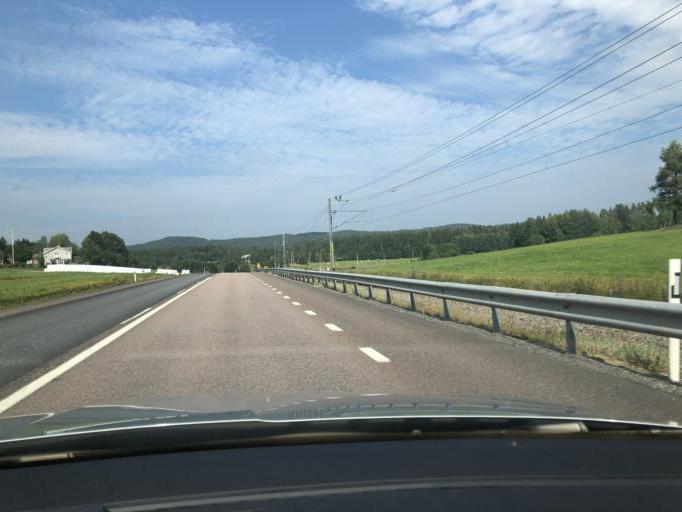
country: SE
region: Vaesternorrland
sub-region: Kramfors Kommun
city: Kramfors
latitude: 62.8230
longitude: 17.8486
